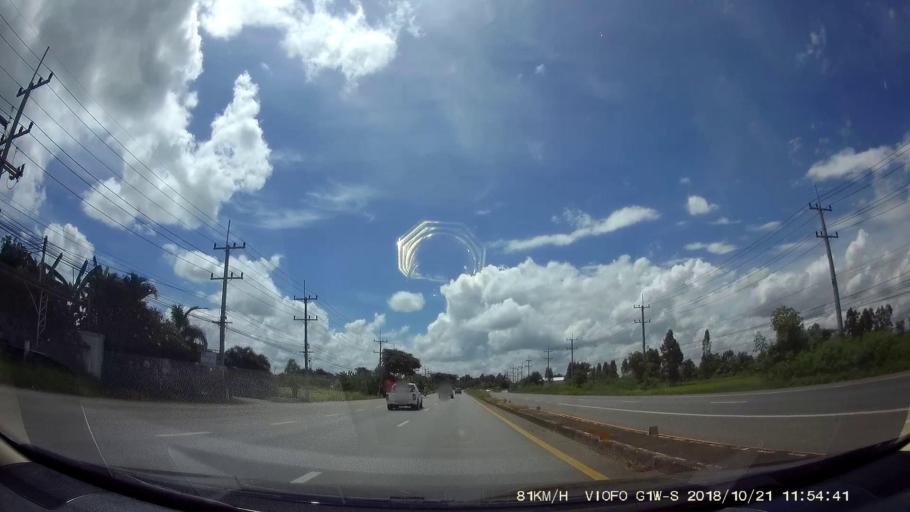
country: TH
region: Chaiyaphum
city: Chatturat
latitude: 15.5821
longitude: 101.8996
